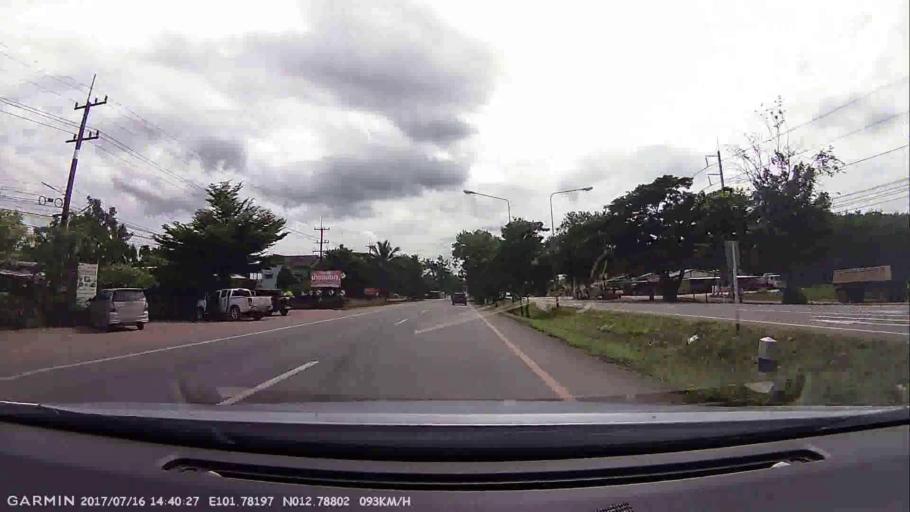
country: TH
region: Chanthaburi
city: Na Yai Am
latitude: 12.7880
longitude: 101.7816
